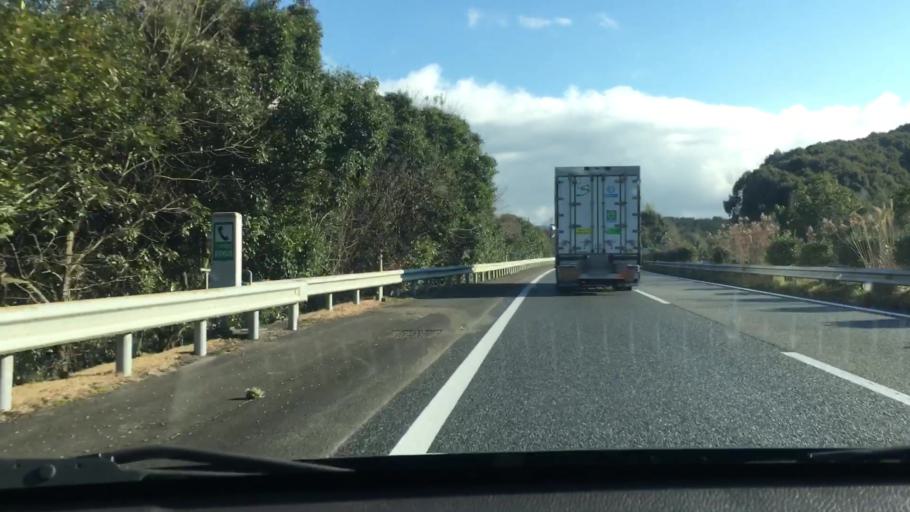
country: JP
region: Kumamoto
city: Hitoyoshi
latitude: 32.1703
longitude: 130.7919
